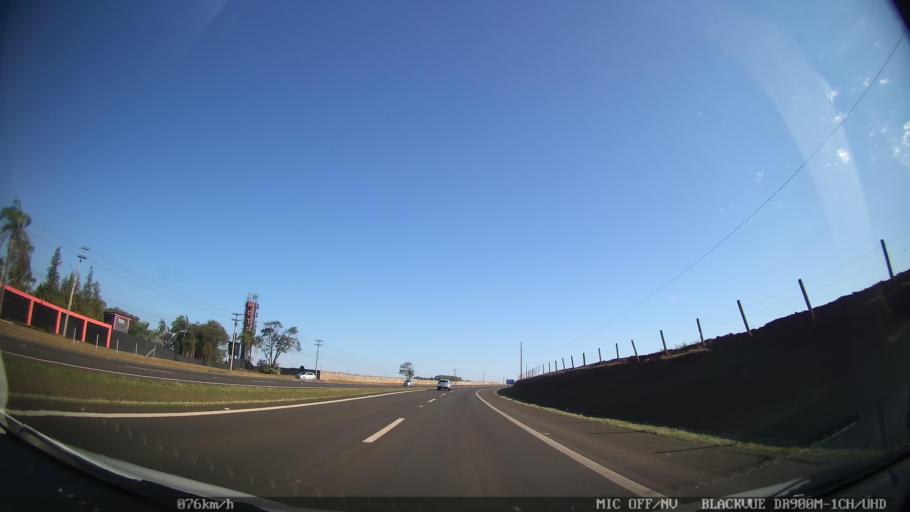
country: BR
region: Sao Paulo
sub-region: Piracicaba
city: Piracicaba
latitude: -22.6871
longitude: -47.6404
